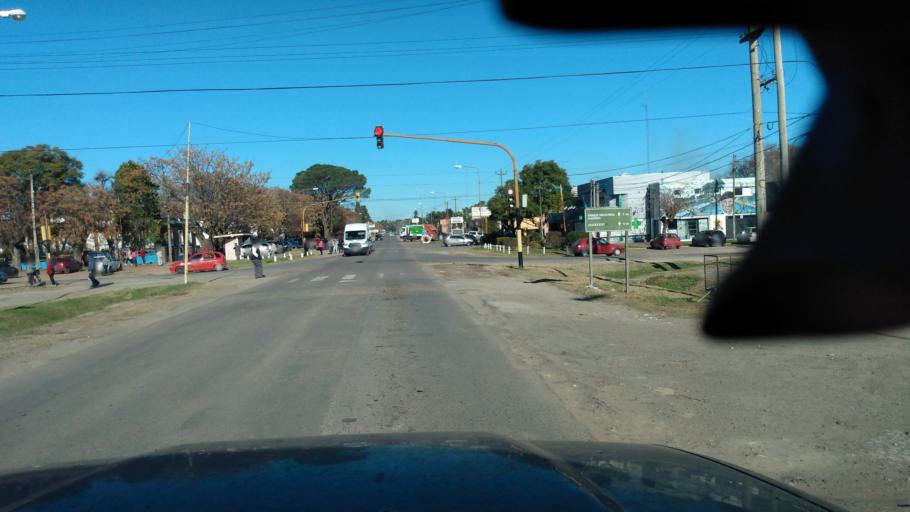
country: AR
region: Buenos Aires
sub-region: Partido de Lujan
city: Lujan
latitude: -34.5707
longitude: -59.1817
